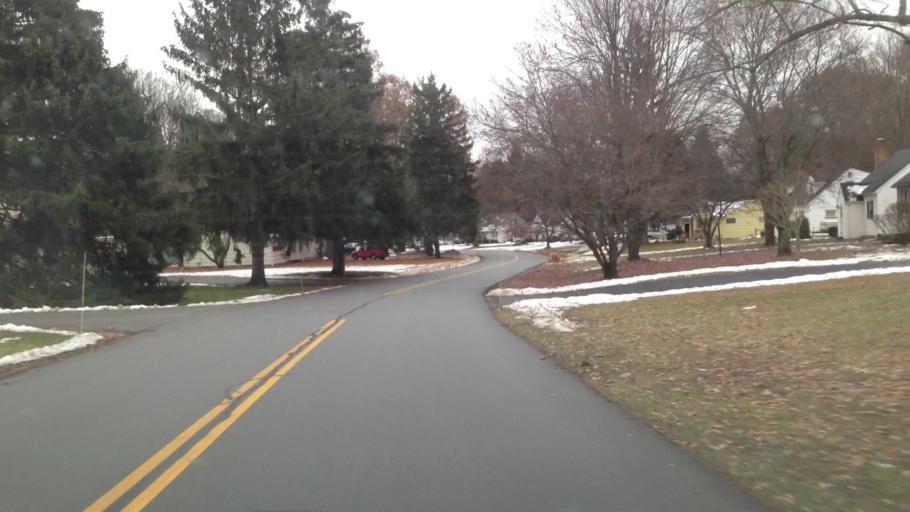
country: US
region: New York
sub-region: Monroe County
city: North Gates
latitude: 43.1245
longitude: -77.7244
